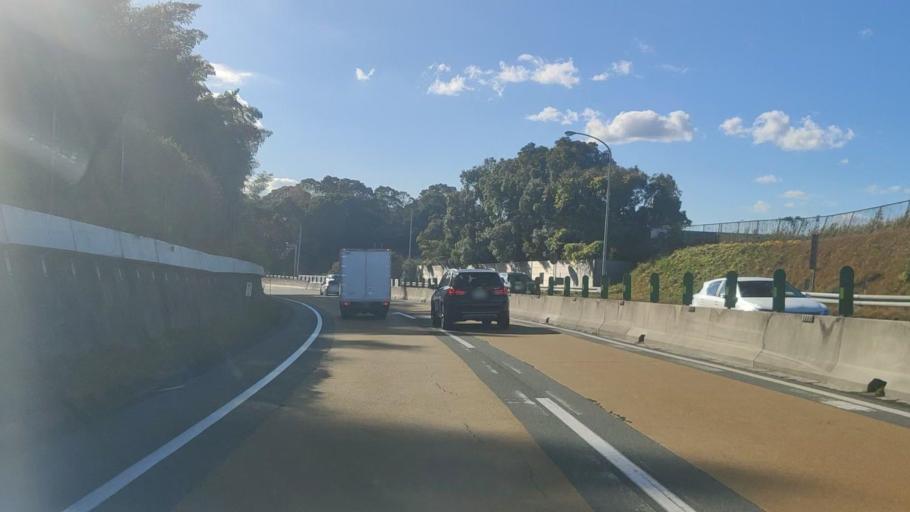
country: JP
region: Fukuoka
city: Kitakyushu
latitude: 33.8503
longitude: 130.7685
